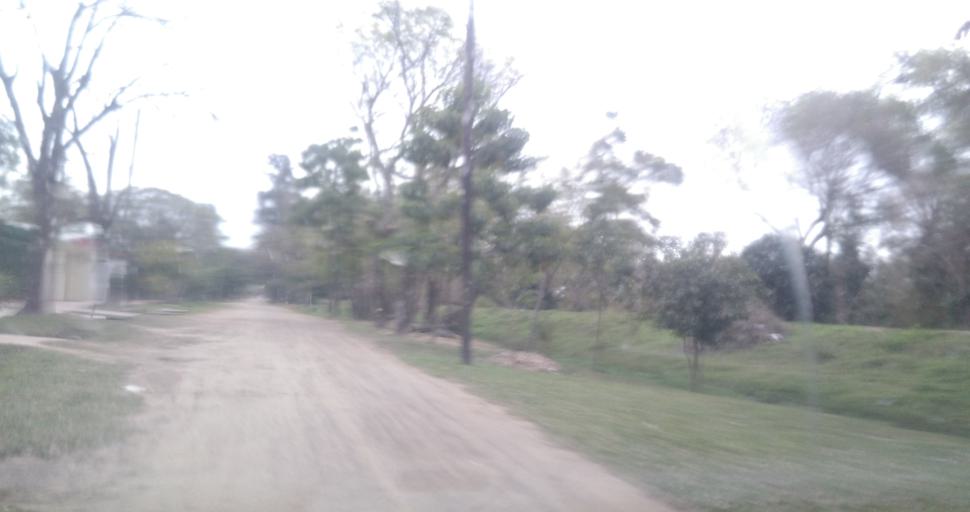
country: AR
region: Chaco
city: Fontana
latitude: -27.4352
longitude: -59.0137
